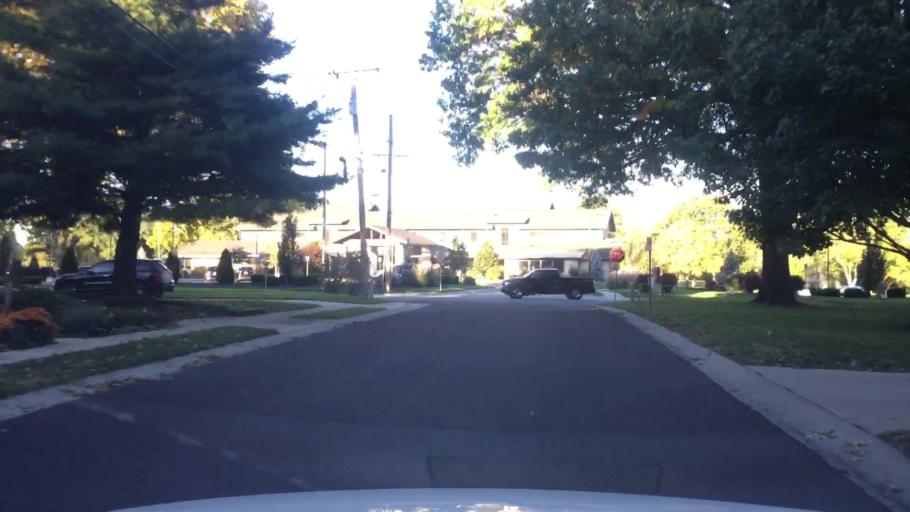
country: US
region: Kansas
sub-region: Johnson County
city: Overland Park
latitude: 39.0041
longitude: -94.6715
